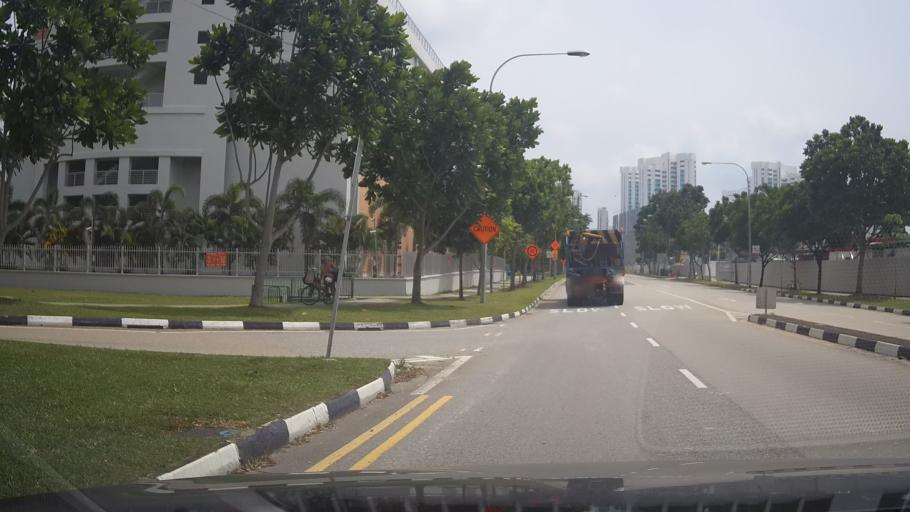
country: SG
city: Singapore
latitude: 1.2975
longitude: 103.8772
